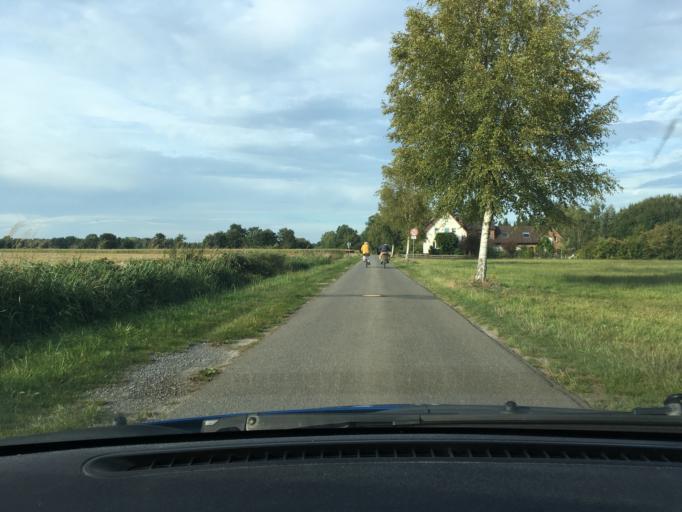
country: DE
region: Lower Saxony
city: Fassberg
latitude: 52.8845
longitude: 10.1206
